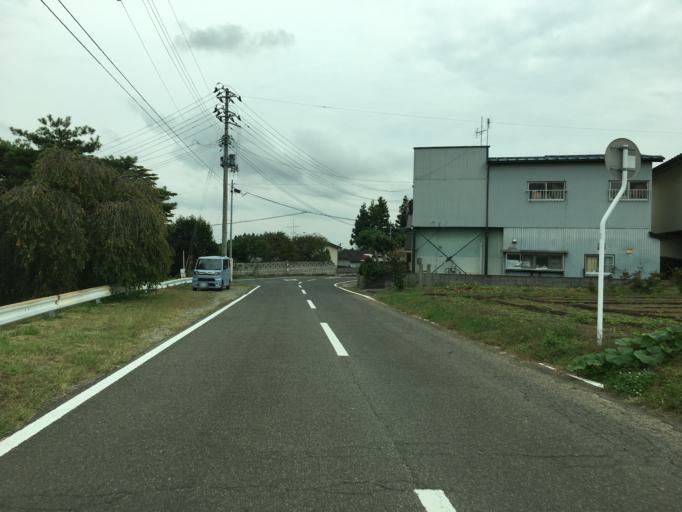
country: JP
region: Fukushima
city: Nihommatsu
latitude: 37.5839
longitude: 140.3905
